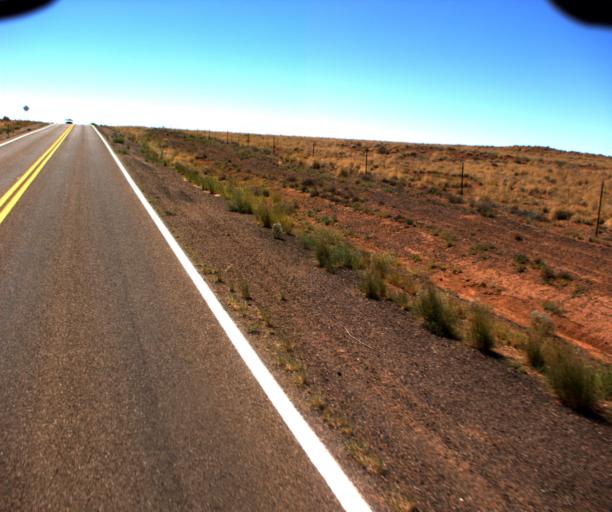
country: US
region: Arizona
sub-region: Navajo County
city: Winslow
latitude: 35.0044
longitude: -110.6899
